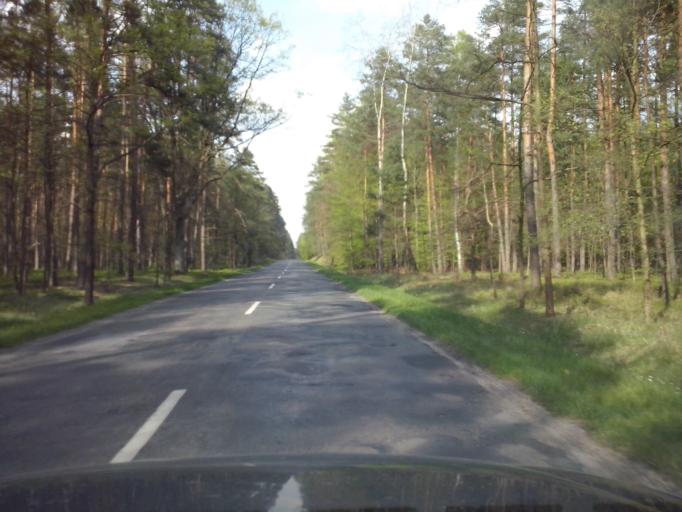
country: PL
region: Subcarpathian Voivodeship
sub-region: Powiat lezajski
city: Letownia
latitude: 50.3782
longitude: 22.2566
